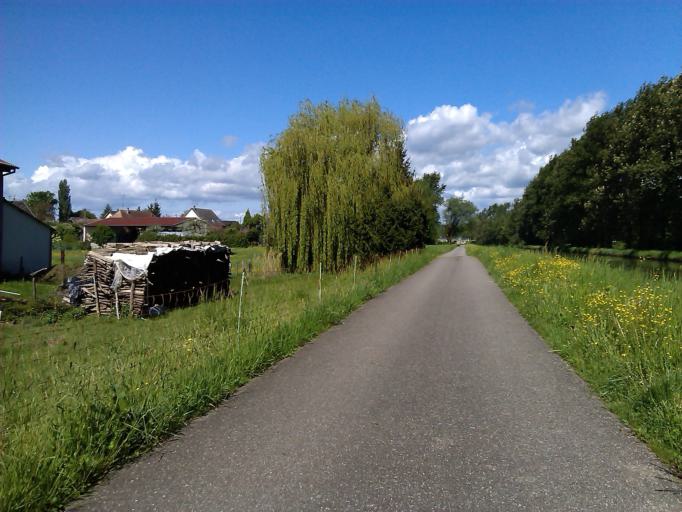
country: FR
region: Alsace
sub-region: Departement du Haut-Rhin
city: Dannemarie
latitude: 47.6323
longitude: 7.0975
